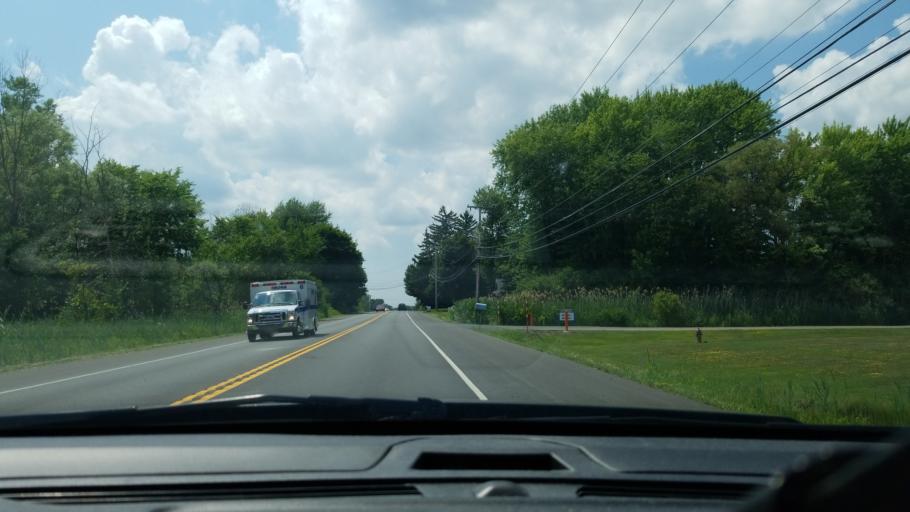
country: US
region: New York
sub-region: Onondaga County
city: Liverpool
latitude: 43.1415
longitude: -76.2004
